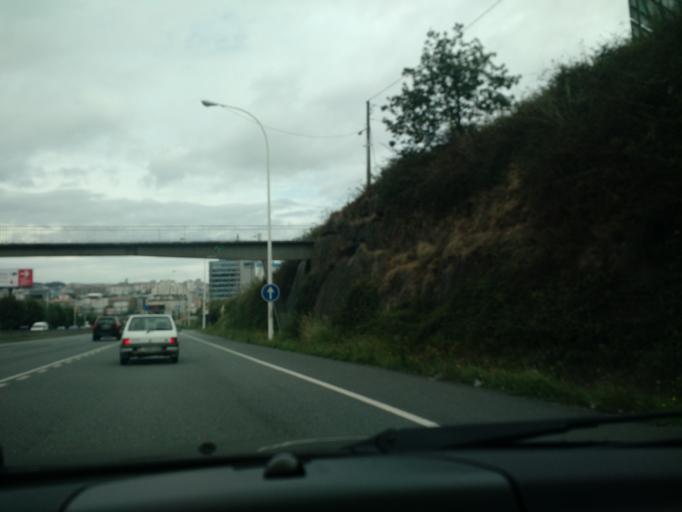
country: ES
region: Galicia
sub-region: Provincia da Coruna
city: A Coruna
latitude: 43.3351
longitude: -8.4028
